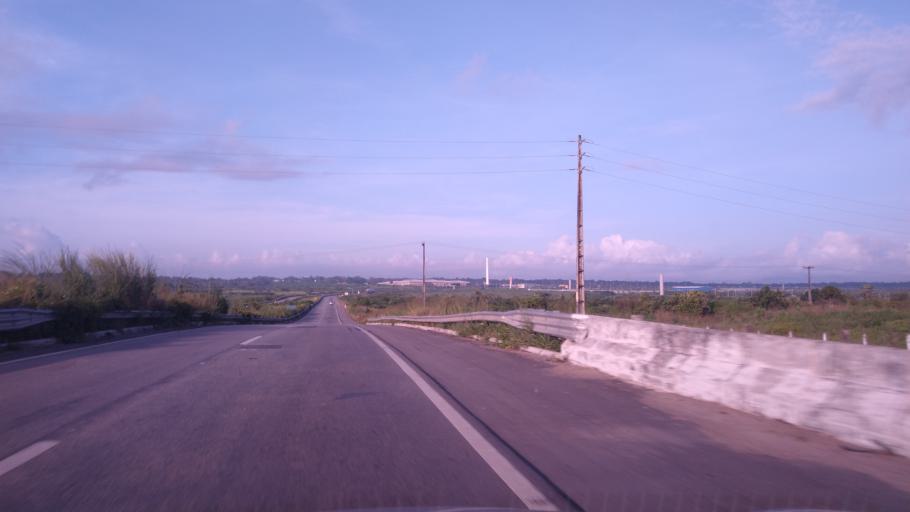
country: BR
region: Ceara
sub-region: Pacajus
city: Pacajus
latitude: -4.1555
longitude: -38.4817
